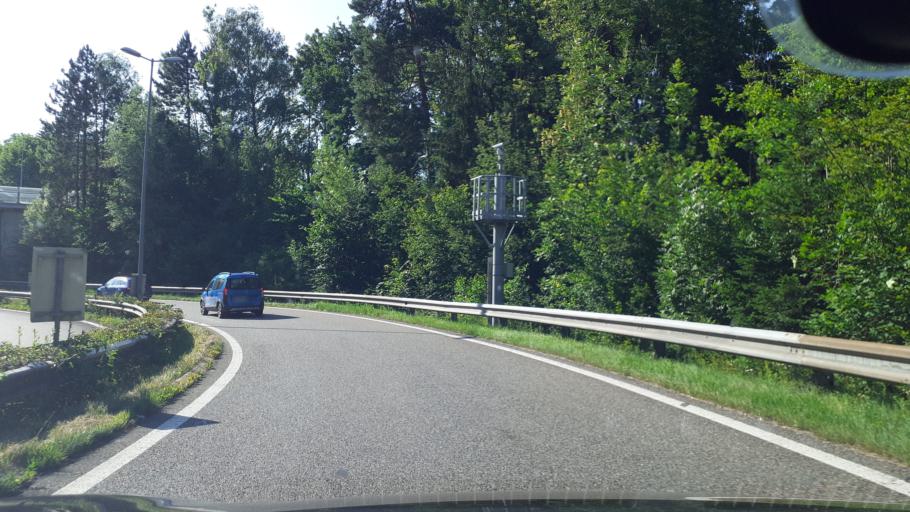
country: AT
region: Vorarlberg
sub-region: Politischer Bezirk Bregenz
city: Lauterach
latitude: 47.4858
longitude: 9.7452
